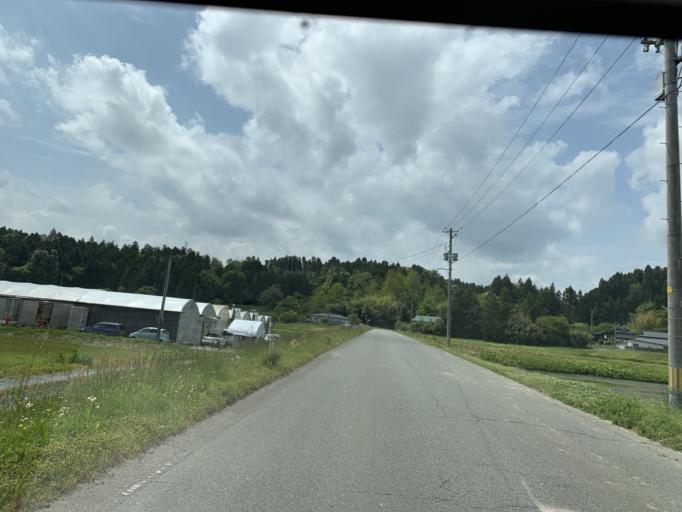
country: JP
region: Miyagi
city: Furukawa
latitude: 38.7399
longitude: 140.9307
